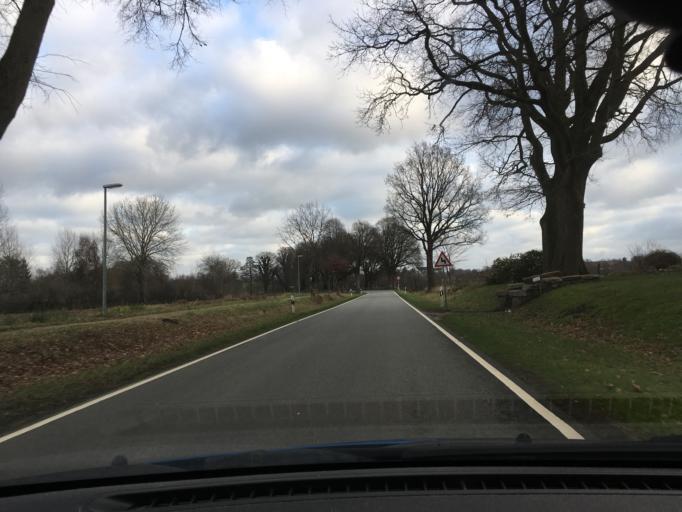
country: DE
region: Schleswig-Holstein
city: Hadenfeld
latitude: 54.0463
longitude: 9.4620
